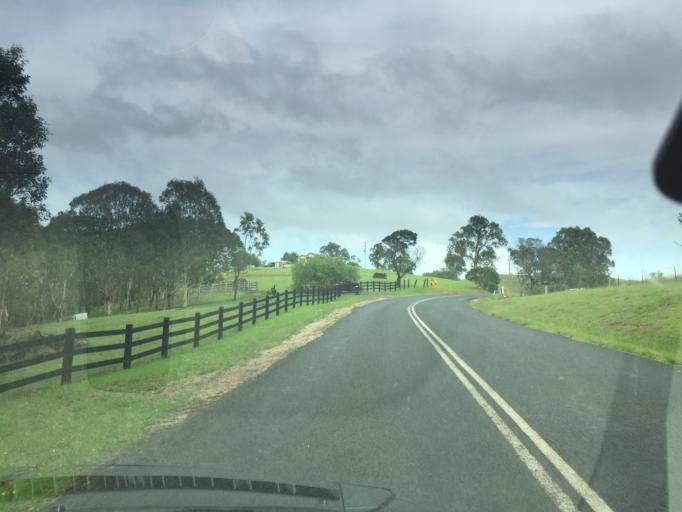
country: AU
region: New South Wales
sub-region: Bega Valley
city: Bega
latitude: -36.7579
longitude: 149.6843
